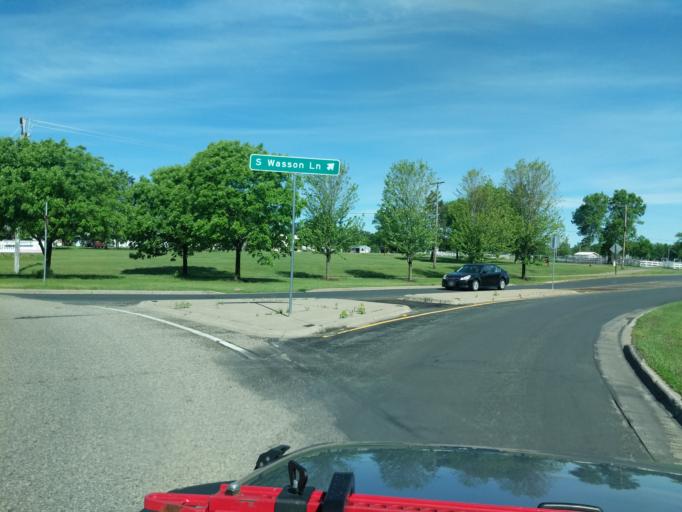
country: US
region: Wisconsin
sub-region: Pierce County
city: River Falls
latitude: 44.8410
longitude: -92.6085
